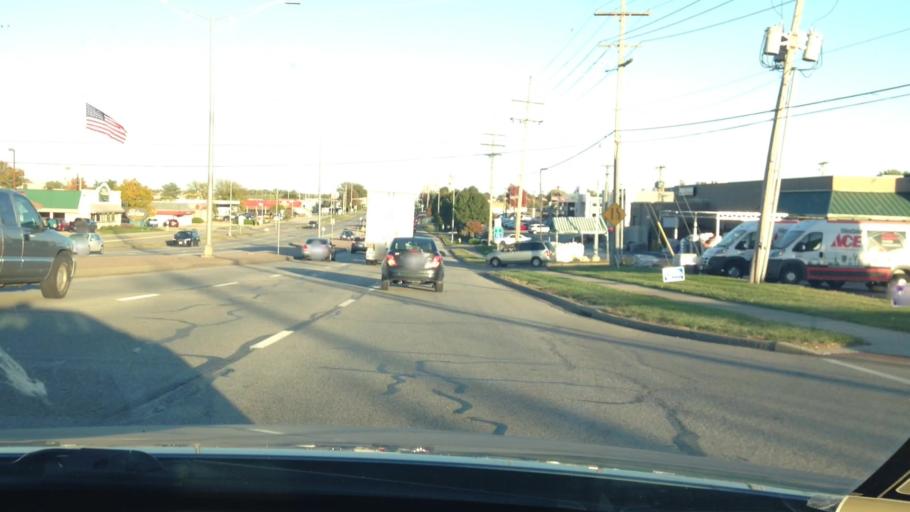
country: US
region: Kansas
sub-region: Johnson County
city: Olathe
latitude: 38.8836
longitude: -94.7888
